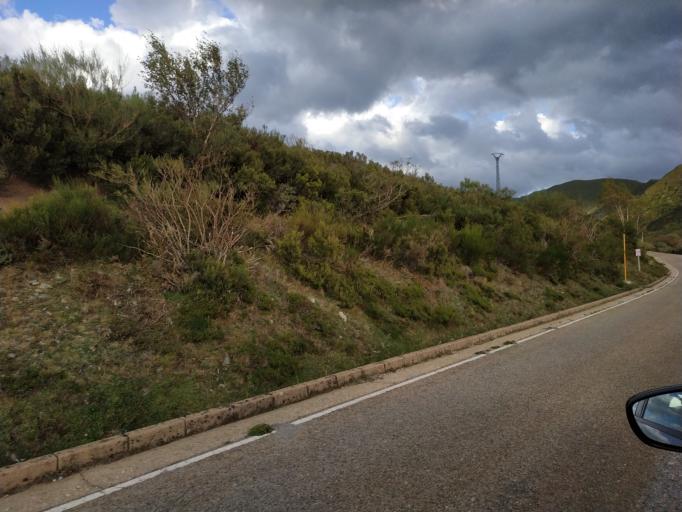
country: ES
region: Castille and Leon
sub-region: Provincia de Leon
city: Candin
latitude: 42.8744
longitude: -6.8274
